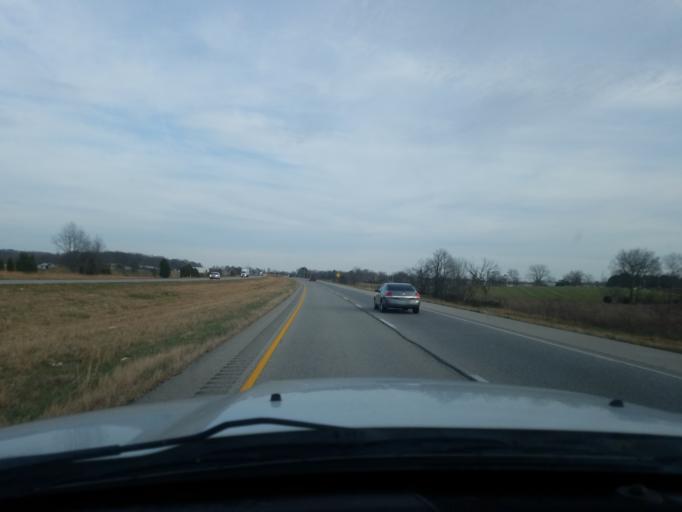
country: US
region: Indiana
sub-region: Harrison County
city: Corydon
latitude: 38.2412
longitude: -86.1882
